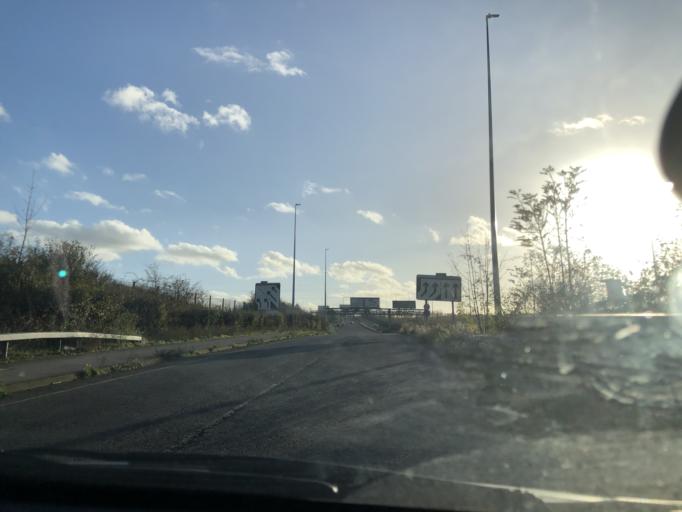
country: GB
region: England
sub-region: Kent
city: Greenhithe
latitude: 51.4391
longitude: 0.2795
